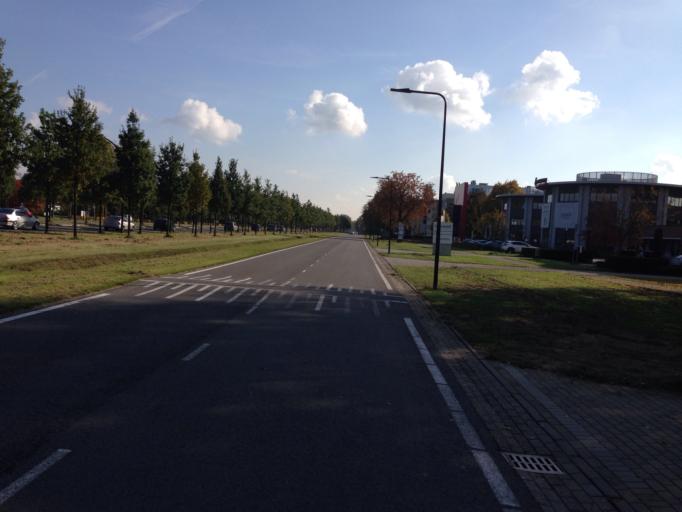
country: NL
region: Overijssel
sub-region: Gemeente Enschede
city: Enschede
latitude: 52.2369
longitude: 6.8522
